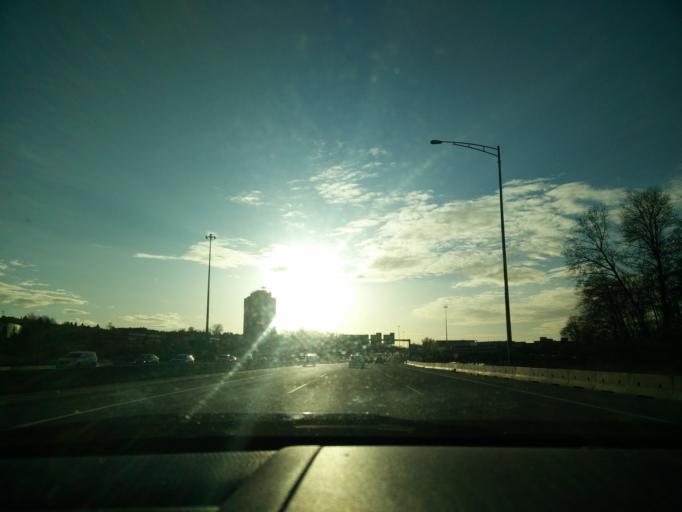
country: CA
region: British Columbia
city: Burnaby
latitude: 49.2579
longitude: -122.9986
